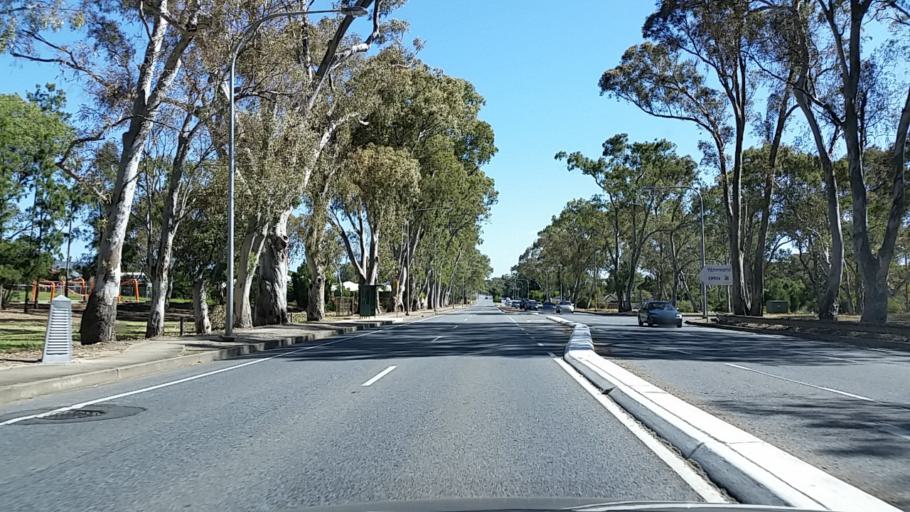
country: AU
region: South Australia
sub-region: Tea Tree Gully
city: Hope Valley
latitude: -34.8209
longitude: 138.6952
